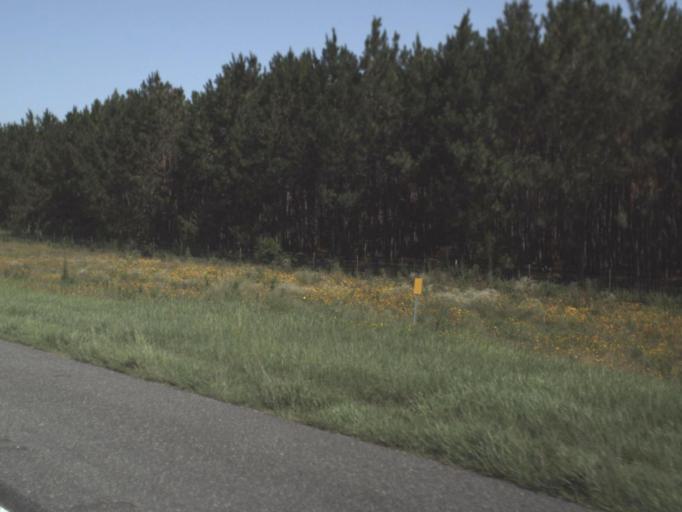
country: US
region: Florida
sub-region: Suwannee County
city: Wellborn
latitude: 30.2893
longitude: -82.8608
